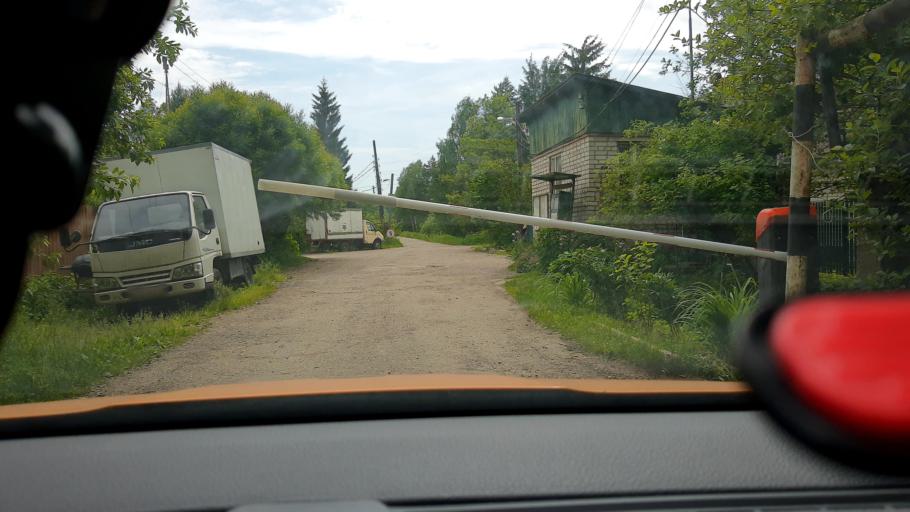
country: RU
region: Moskovskaya
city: Chupryakovo
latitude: 55.5662
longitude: 36.6601
